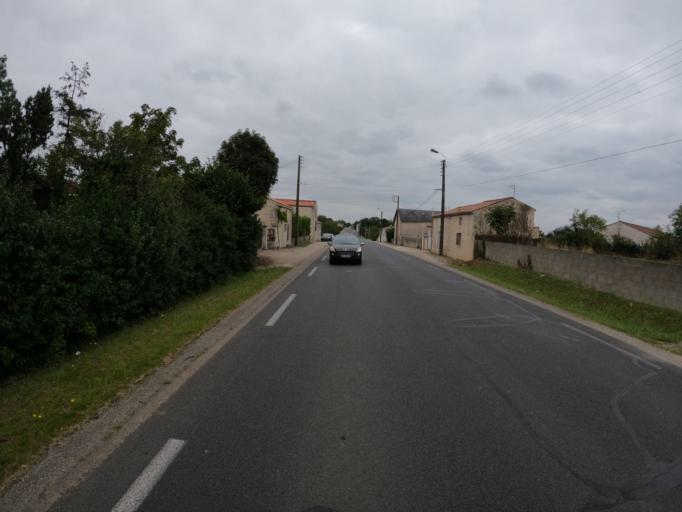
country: FR
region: Pays de la Loire
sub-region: Departement de la Vendee
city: Saint-Hilaire-des-Loges
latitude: 46.4040
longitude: -0.6737
